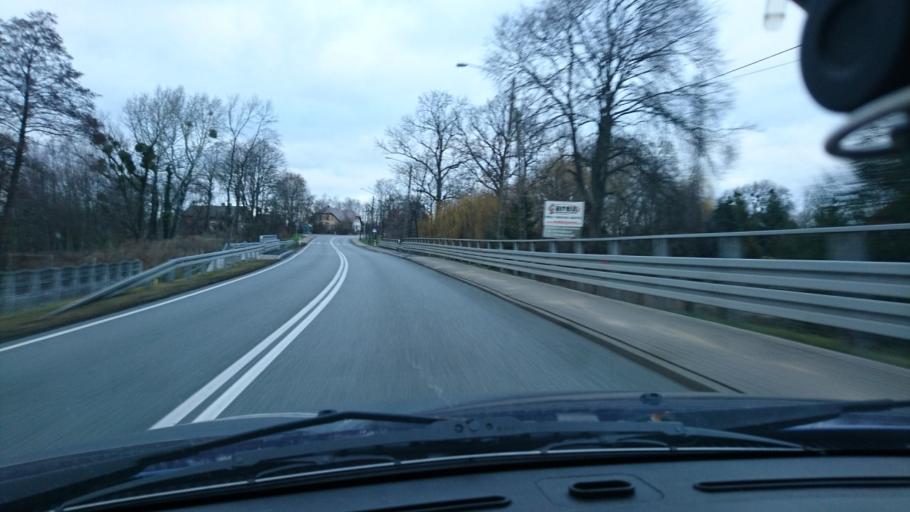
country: PL
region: Opole Voivodeship
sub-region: Powiat kluczborski
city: Byczyna
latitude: 51.0622
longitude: 18.2009
